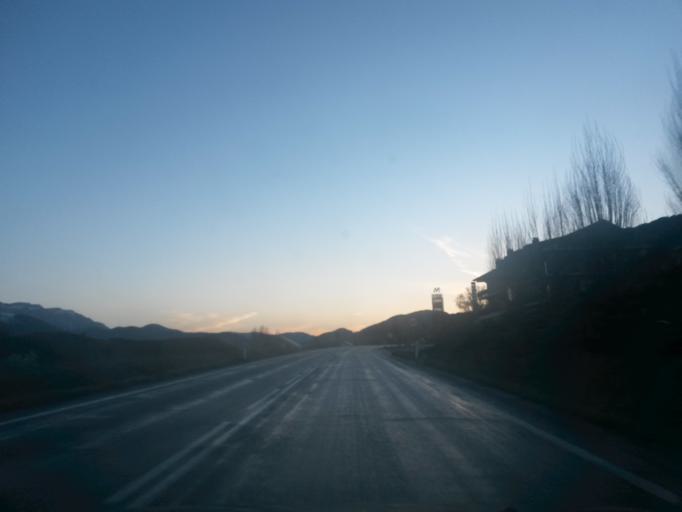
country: ES
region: Catalonia
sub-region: Provincia de Lleida
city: Bellver de Cerdanya
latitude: 42.3729
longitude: 1.7629
